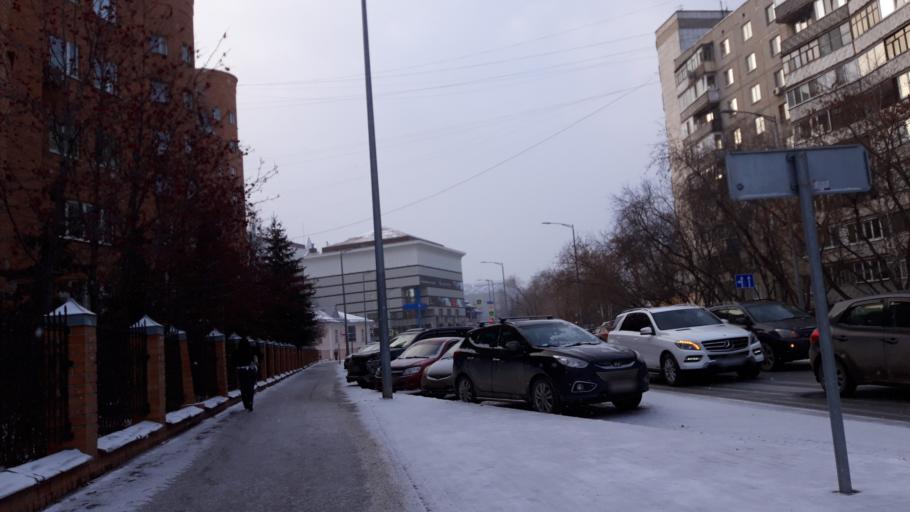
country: RU
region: Tjumen
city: Tyumen
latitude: 57.1557
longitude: 65.5511
